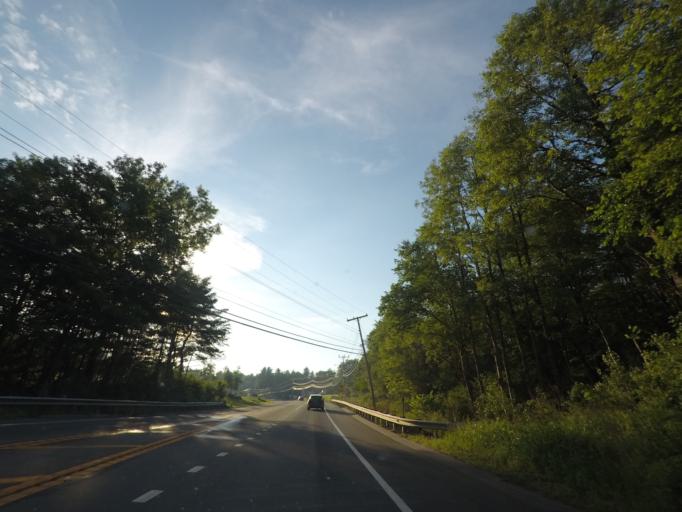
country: US
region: Massachusetts
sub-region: Worcester County
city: Fiskdale
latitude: 42.1117
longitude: -72.1489
